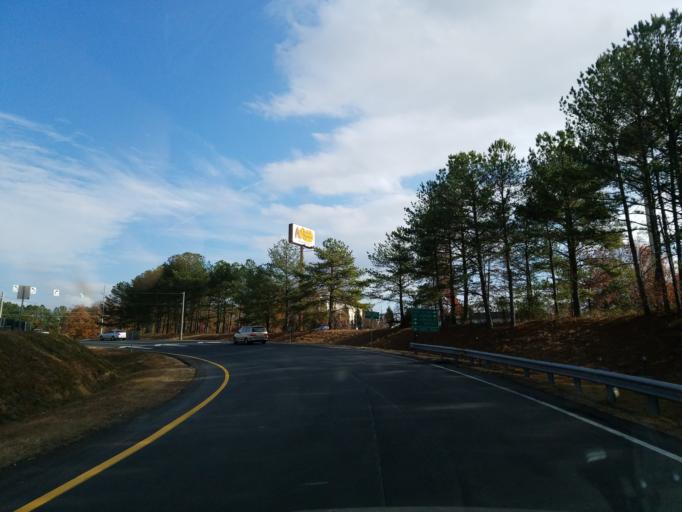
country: US
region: Georgia
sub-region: Cobb County
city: Austell
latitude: 33.7757
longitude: -84.6066
